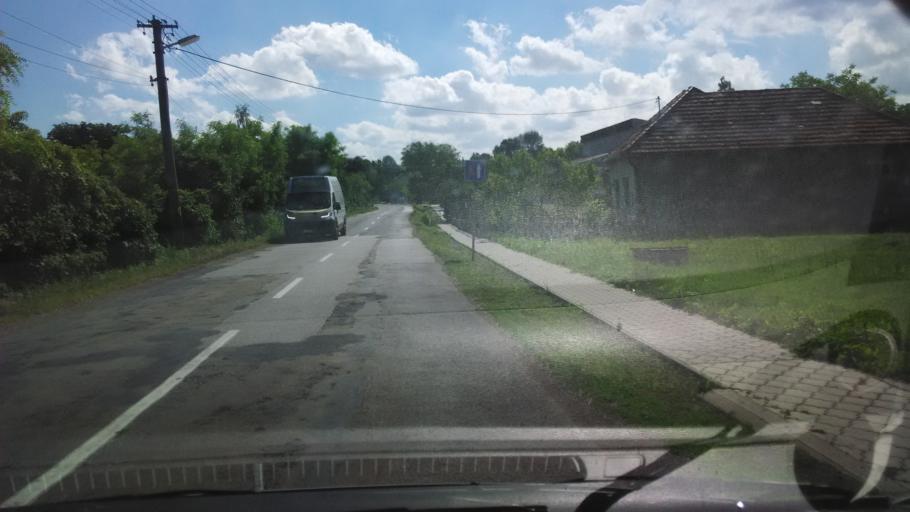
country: SK
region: Nitriansky
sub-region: Okres Nitra
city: Vrable
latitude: 48.1429
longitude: 18.4037
